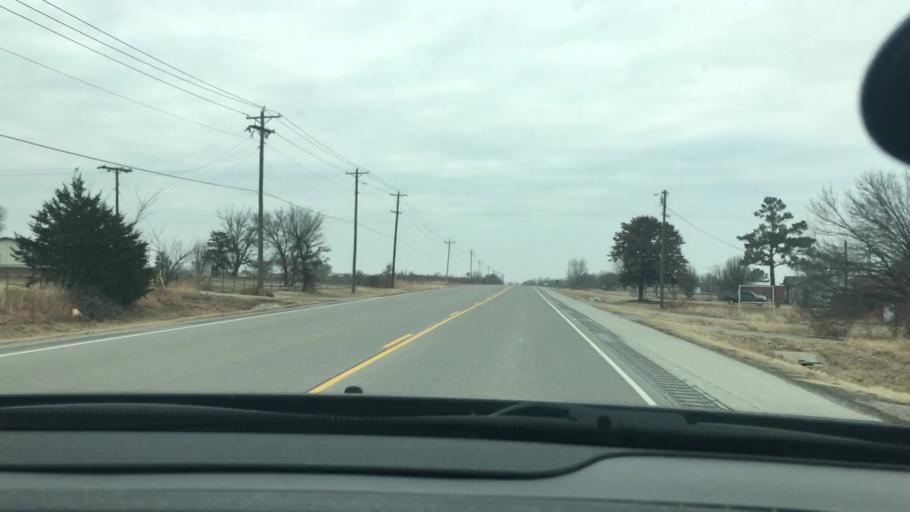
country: US
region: Oklahoma
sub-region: Carter County
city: Healdton
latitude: 34.3988
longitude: -97.5051
